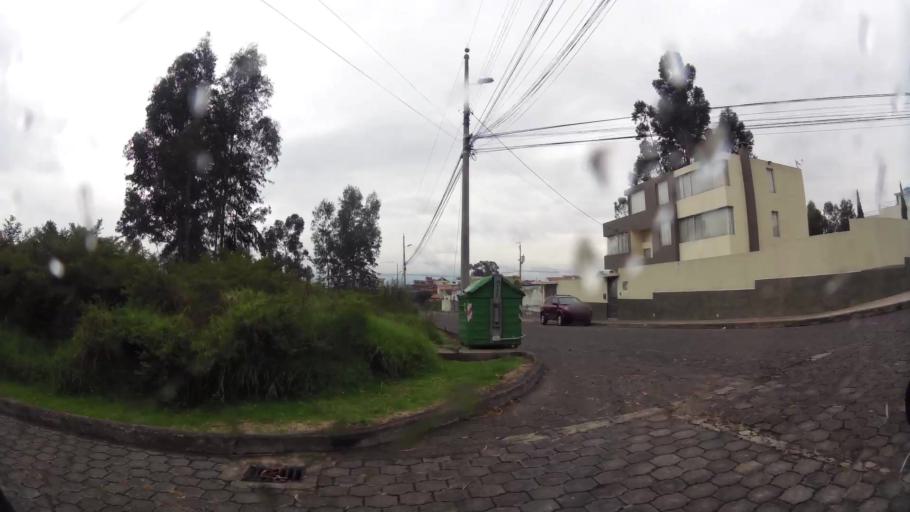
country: EC
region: Pichincha
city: Sangolqui
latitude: -0.3240
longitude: -78.4323
